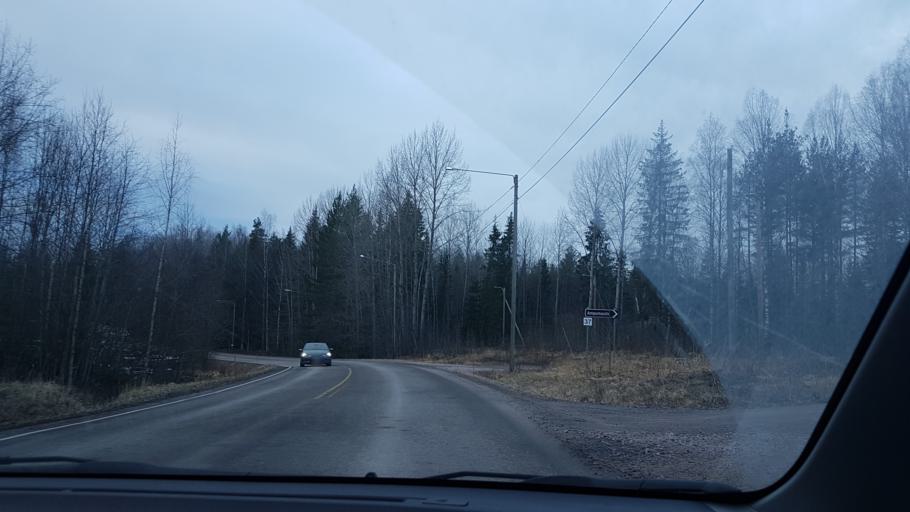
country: FI
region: Uusimaa
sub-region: Helsinki
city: Kauniainen
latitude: 60.3432
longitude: 24.7156
